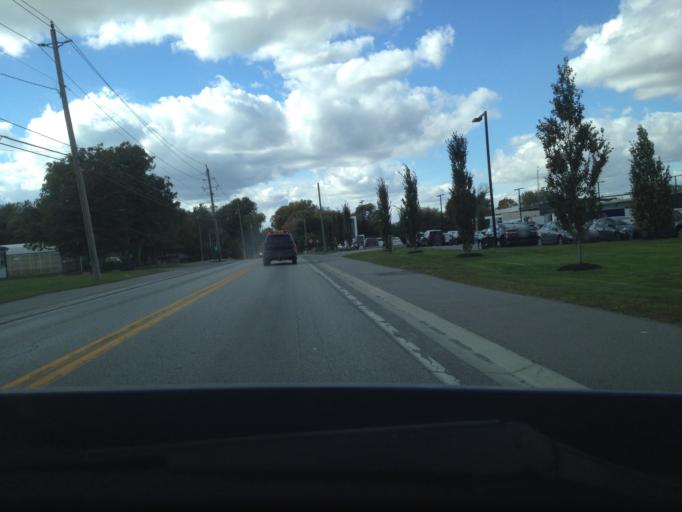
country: CA
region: Ontario
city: Amherstburg
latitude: 42.0397
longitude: -82.6586
